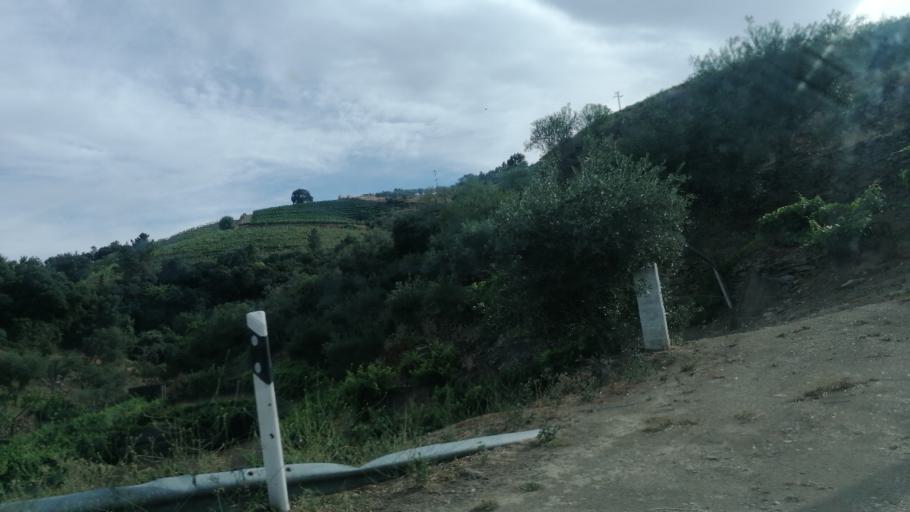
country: PT
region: Viseu
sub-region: Sao Joao da Pesqueira
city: Sao Joao da Pesqueira
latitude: 41.0800
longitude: -7.3931
